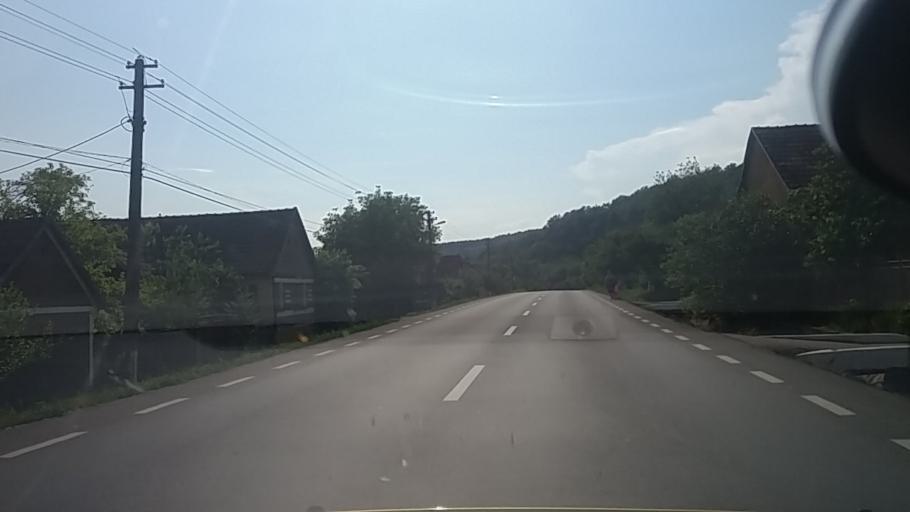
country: RO
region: Arad
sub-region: Comuna Ususau
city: Ususau
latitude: 46.1117
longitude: 21.8262
